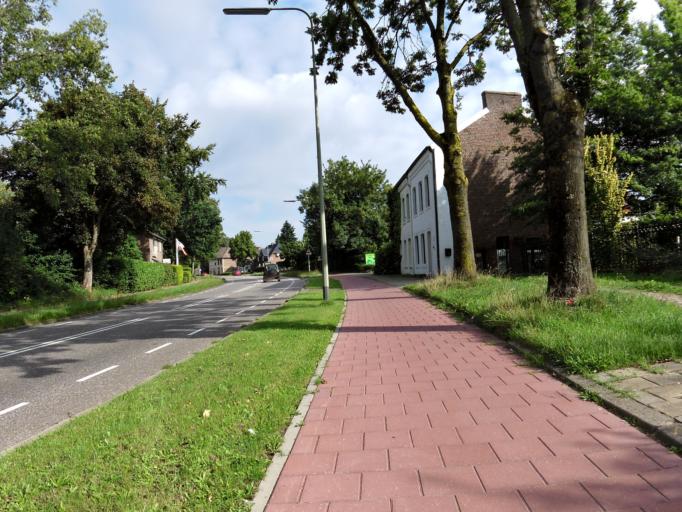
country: NL
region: Limburg
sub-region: Gemeente Kerkrade
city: Kerkrade
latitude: 50.9048
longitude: 6.0581
